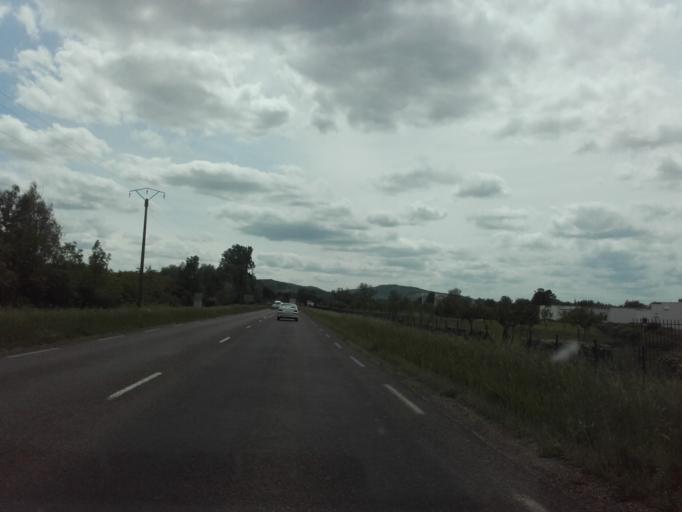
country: FR
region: Bourgogne
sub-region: Departement de la Cote-d'Or
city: Corpeau
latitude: 46.9318
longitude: 4.7505
